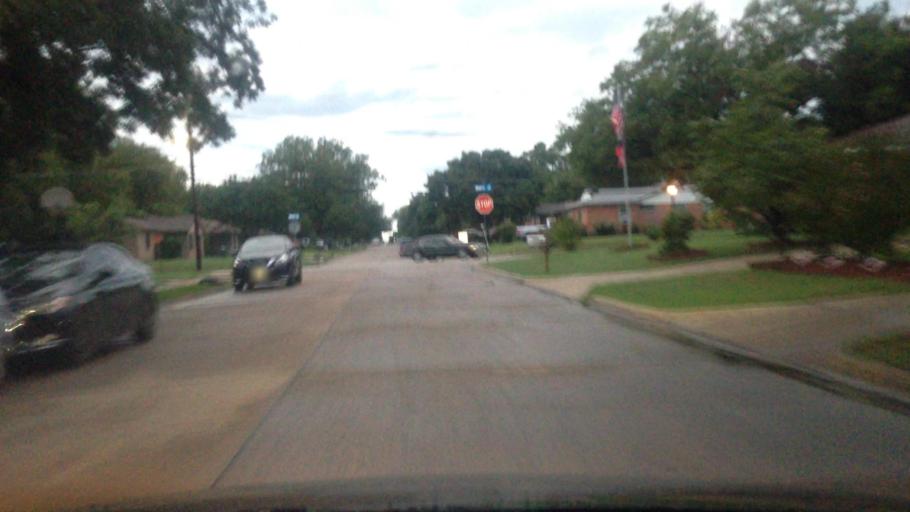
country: US
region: Texas
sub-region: Tarrant County
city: Arlington
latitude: 32.7321
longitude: -97.0710
